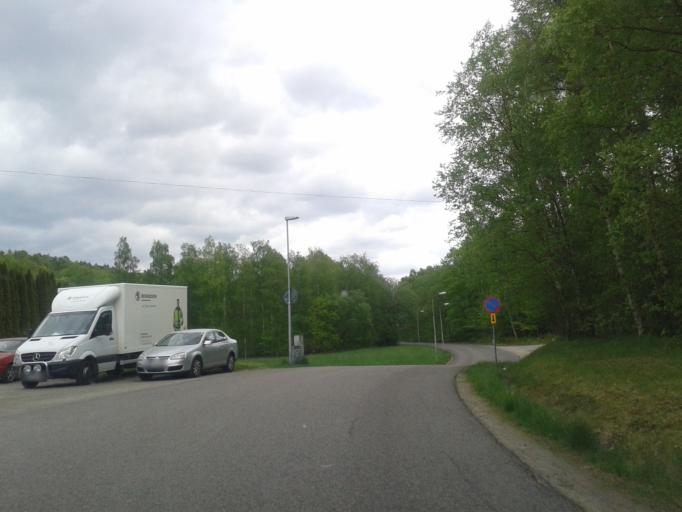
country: SE
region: Vaestra Goetaland
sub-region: Kungalvs Kommun
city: Kungalv
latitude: 57.8683
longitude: 11.9950
